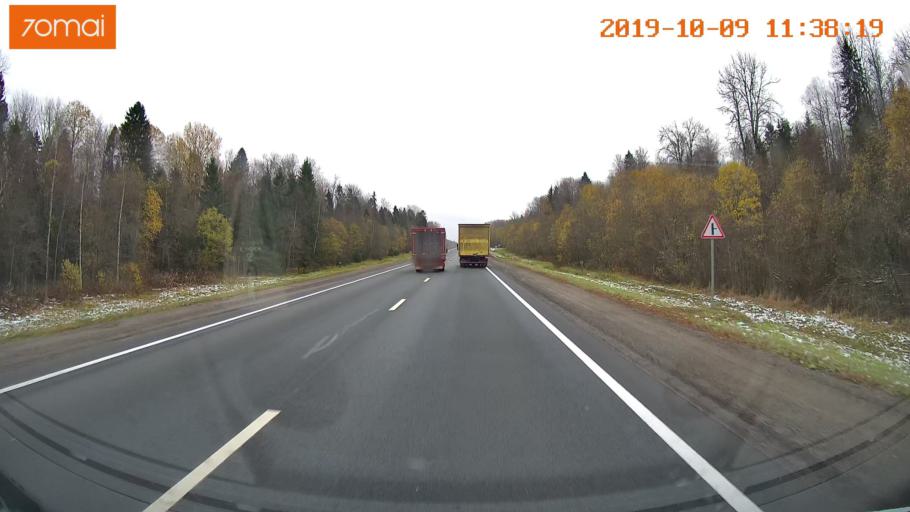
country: RU
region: Vologda
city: Gryazovets
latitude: 58.9695
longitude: 40.1546
